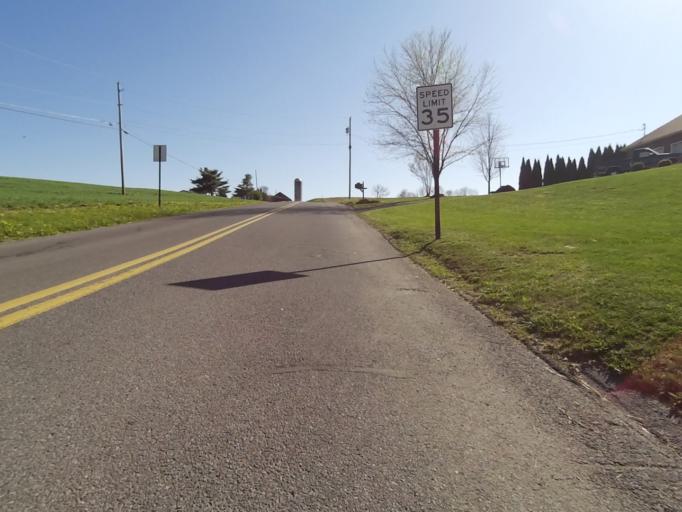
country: US
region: Pennsylvania
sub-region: Centre County
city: Bellefonte
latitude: 40.8899
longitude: -77.8059
